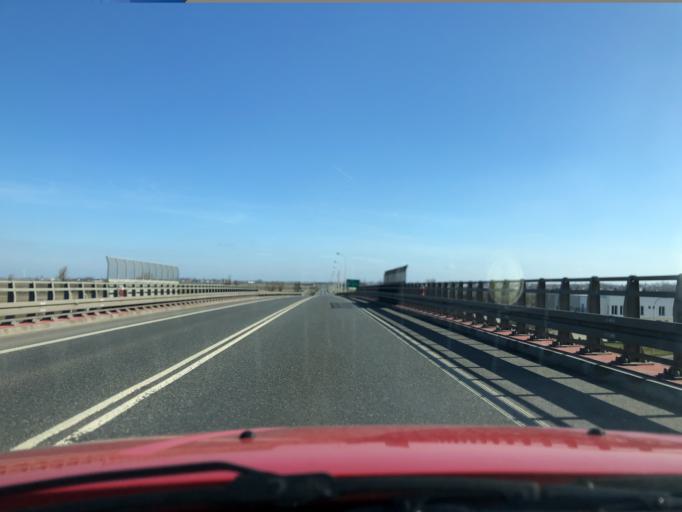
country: PL
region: Greater Poland Voivodeship
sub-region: Powiat ostrowski
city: Skalmierzyce
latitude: 51.6997
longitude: 17.9532
